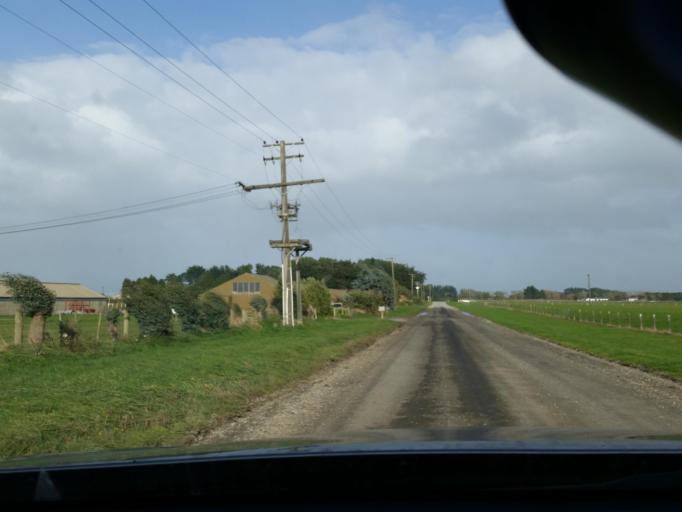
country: NZ
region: Southland
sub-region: Invercargill City
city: Invercargill
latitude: -46.3059
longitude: 168.3034
